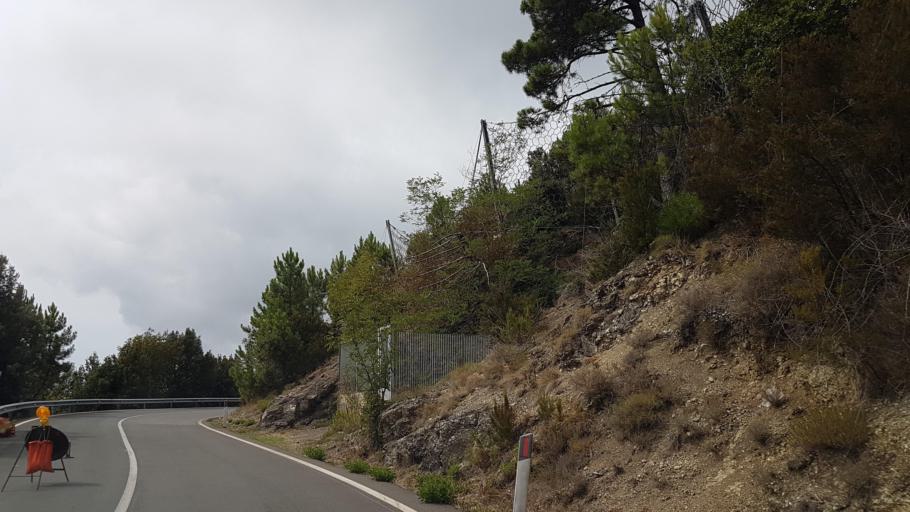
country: IT
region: Liguria
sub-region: Provincia di La Spezia
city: Framura
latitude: 44.2521
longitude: 9.5623
